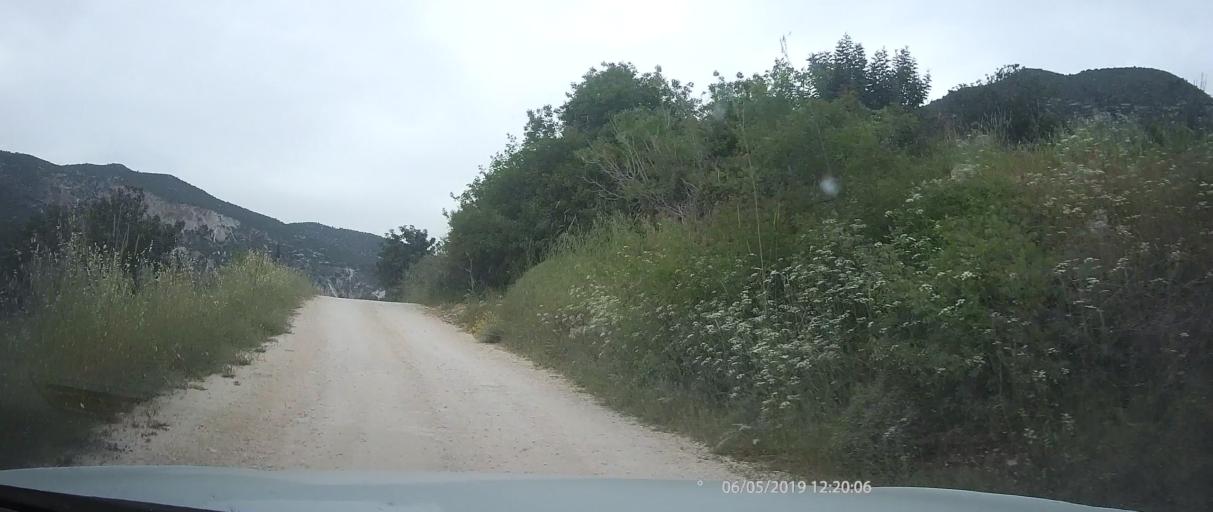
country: CY
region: Pafos
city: Tala
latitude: 34.8610
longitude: 32.4305
